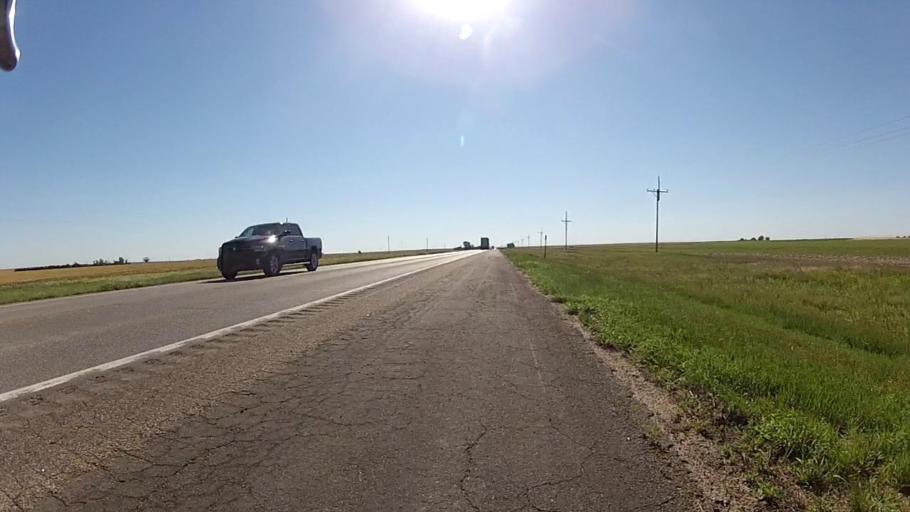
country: US
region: Kansas
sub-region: Kiowa County
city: Greensburg
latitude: 37.5862
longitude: -99.6551
